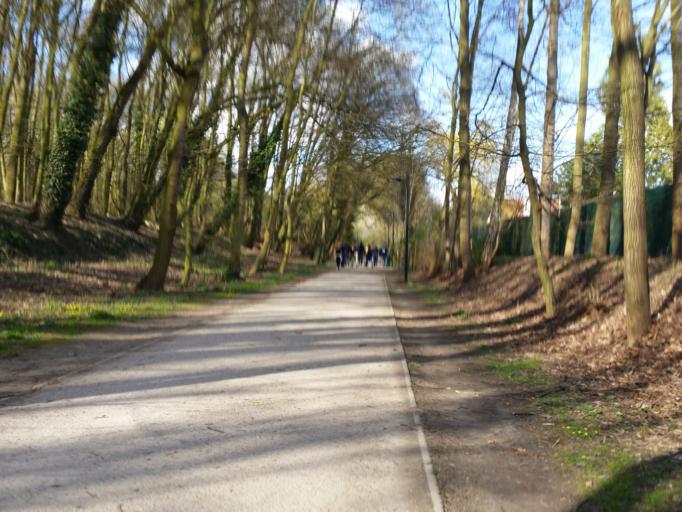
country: BE
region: Flanders
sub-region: Provincie Vlaams-Brabant
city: Kraainem
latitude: 50.8236
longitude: 4.4287
